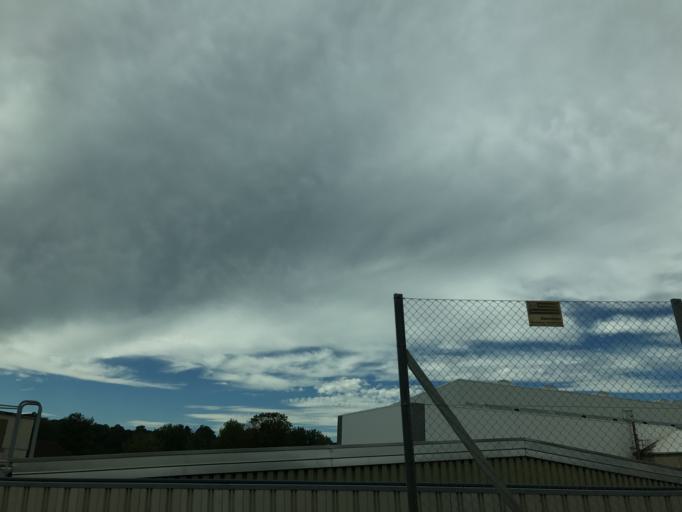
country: DE
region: Baden-Wuerttemberg
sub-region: Tuebingen Region
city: Ravensburg
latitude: 47.7887
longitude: 9.6114
